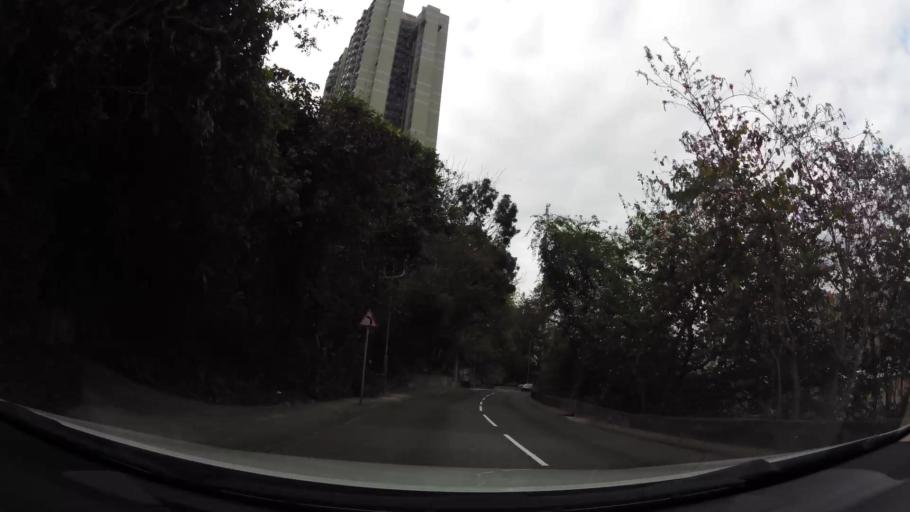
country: HK
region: Wanchai
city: Wan Chai
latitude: 22.2696
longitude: 114.1785
